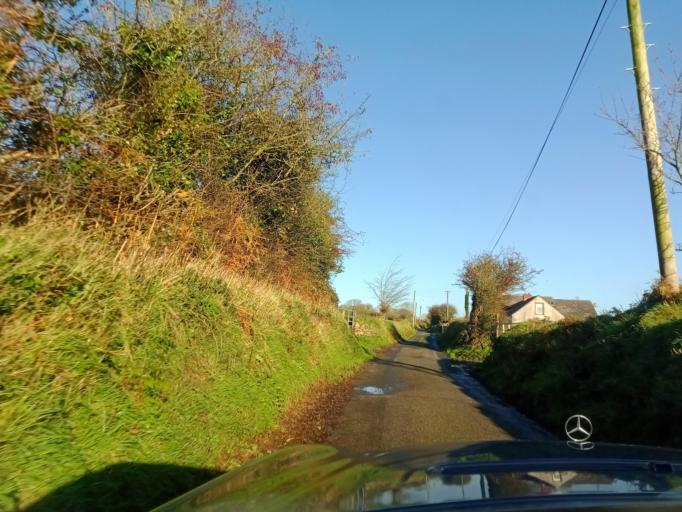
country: IE
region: Leinster
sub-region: Kilkenny
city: Mooncoin
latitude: 52.2956
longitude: -7.2080
